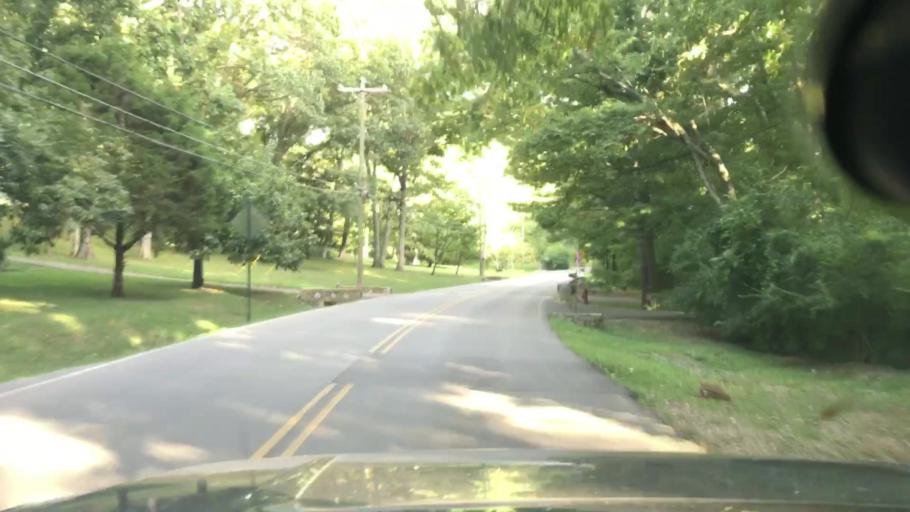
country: US
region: Tennessee
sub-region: Davidson County
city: Forest Hills
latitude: 36.0505
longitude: -86.8416
